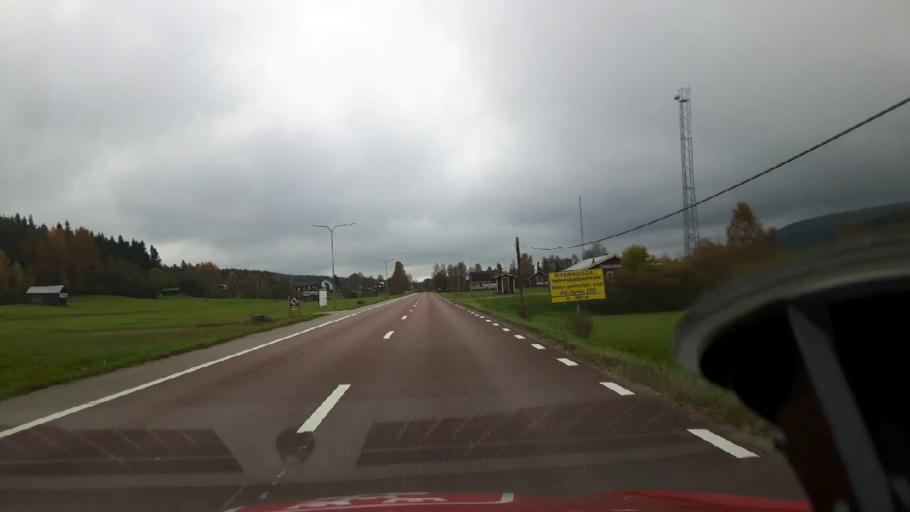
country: SE
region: Jaemtland
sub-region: Harjedalens Kommun
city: Sveg
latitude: 62.2864
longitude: 14.7969
